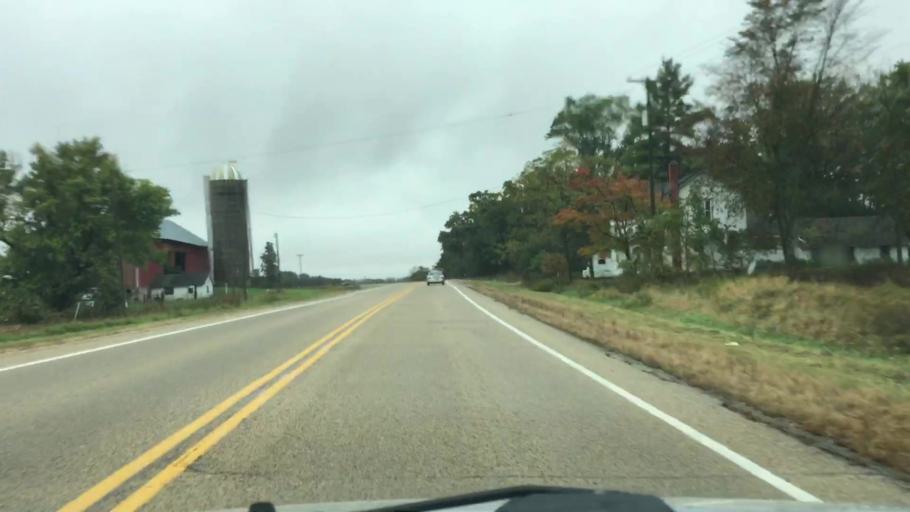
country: US
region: Wisconsin
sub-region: Jefferson County
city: Palmyra
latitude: 42.8731
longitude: -88.6411
